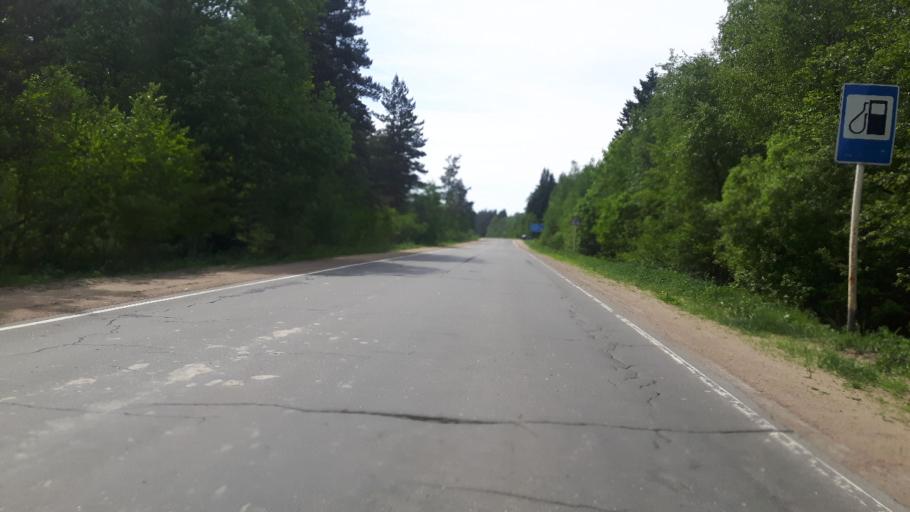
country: RU
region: Leningrad
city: Ust'-Luga
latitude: 59.6392
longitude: 28.2885
